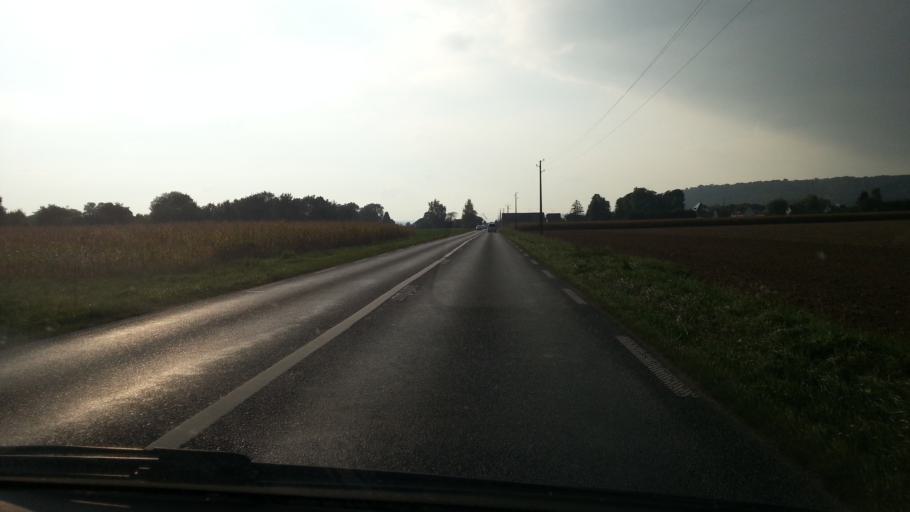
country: FR
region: Picardie
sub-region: Departement de l'Oise
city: Noyon
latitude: 49.5821
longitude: 3.0631
